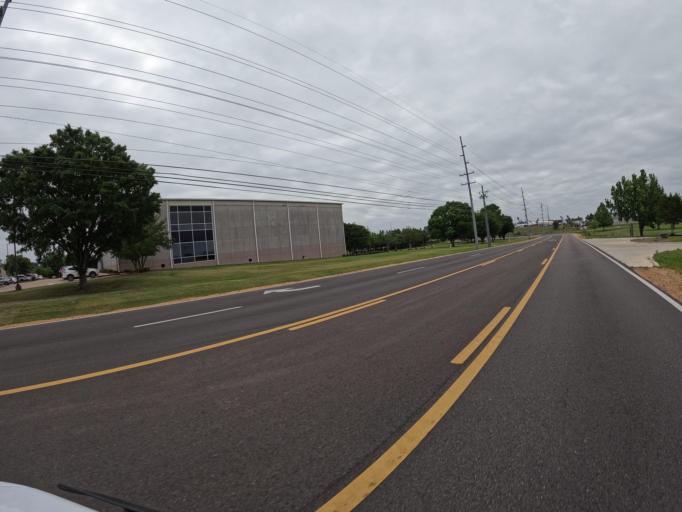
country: US
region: Mississippi
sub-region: Lee County
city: Tupelo
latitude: 34.2666
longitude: -88.7642
